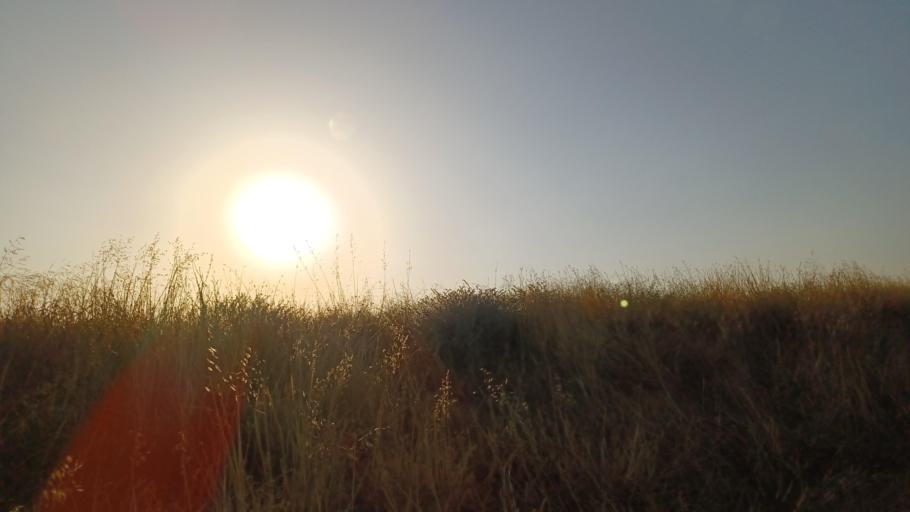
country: CY
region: Larnaka
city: Athienou
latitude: 35.0535
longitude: 33.4995
